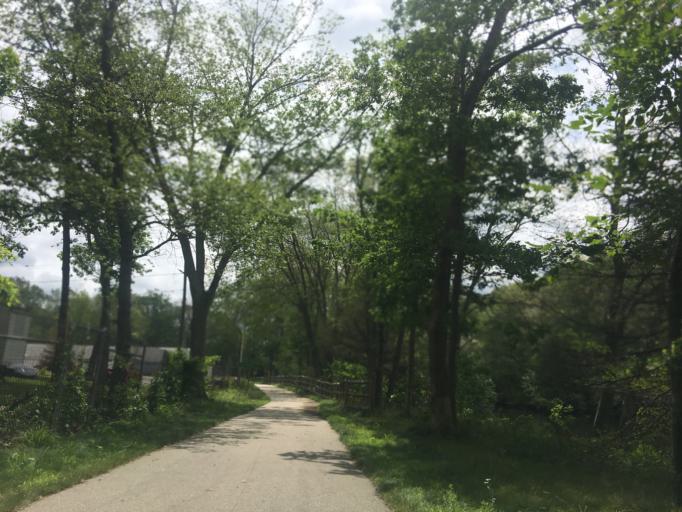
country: US
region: Connecticut
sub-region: Windham County
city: East Brooklyn
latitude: 41.7904
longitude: -71.8895
